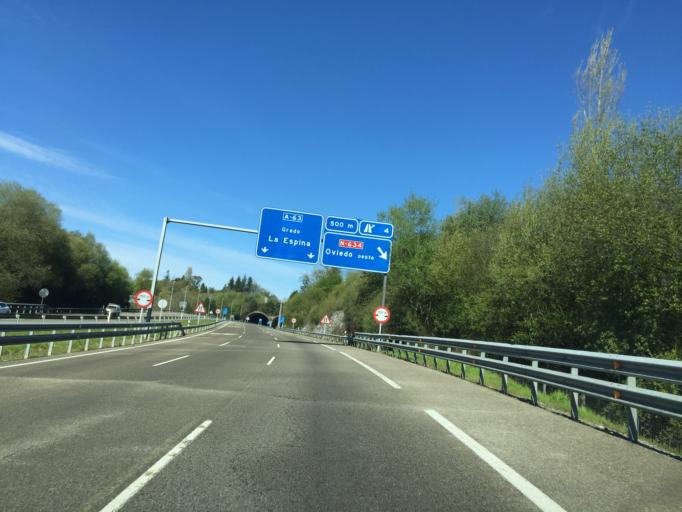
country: ES
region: Asturias
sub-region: Province of Asturias
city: Oviedo
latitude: 43.3437
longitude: -5.8869
